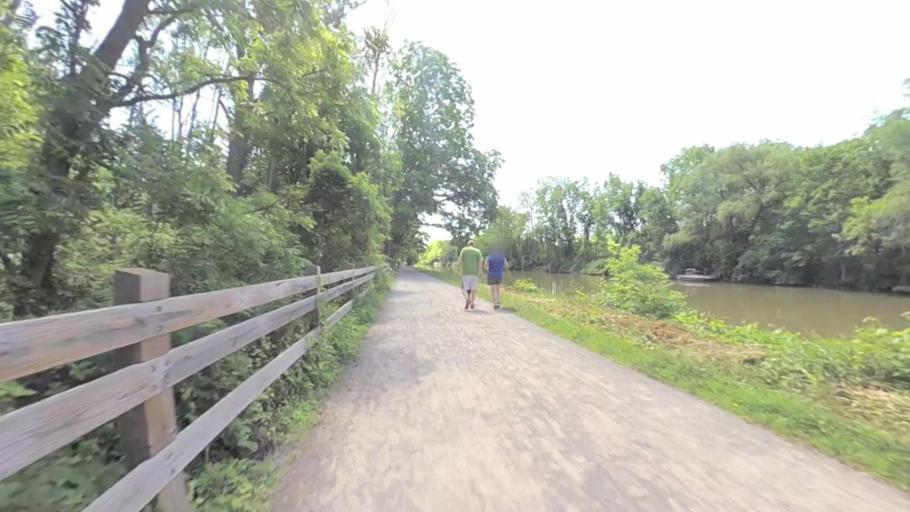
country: US
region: New York
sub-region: Monroe County
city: Pittsford
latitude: 43.0868
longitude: -77.5088
